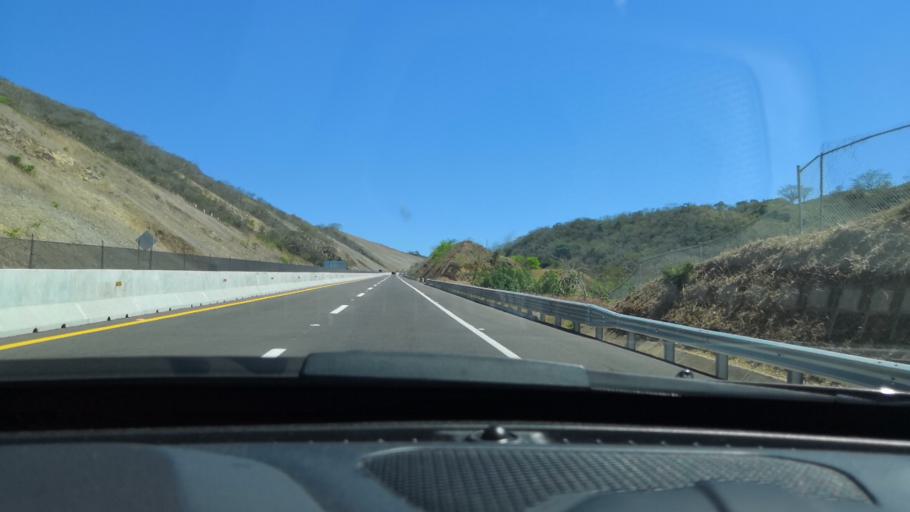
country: MX
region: Nayarit
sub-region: Compostela
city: Juan Escutia (Borbollon)
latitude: 21.1272
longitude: -104.8964
